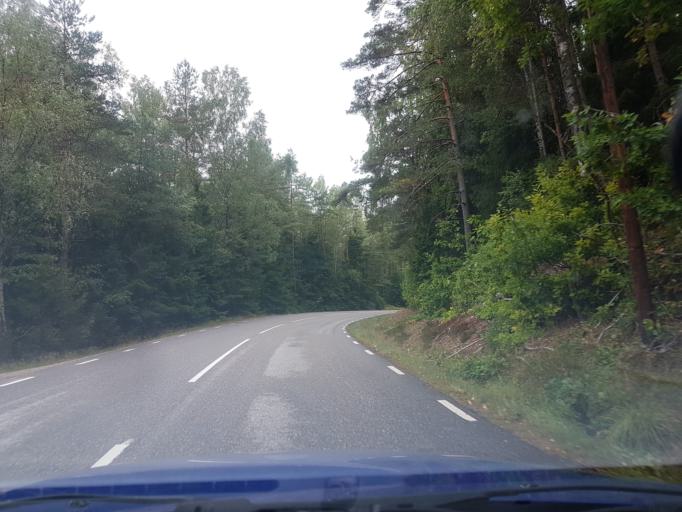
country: SE
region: Vaestra Goetaland
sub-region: Lerums Kommun
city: Grabo
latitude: 57.9182
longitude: 12.3265
